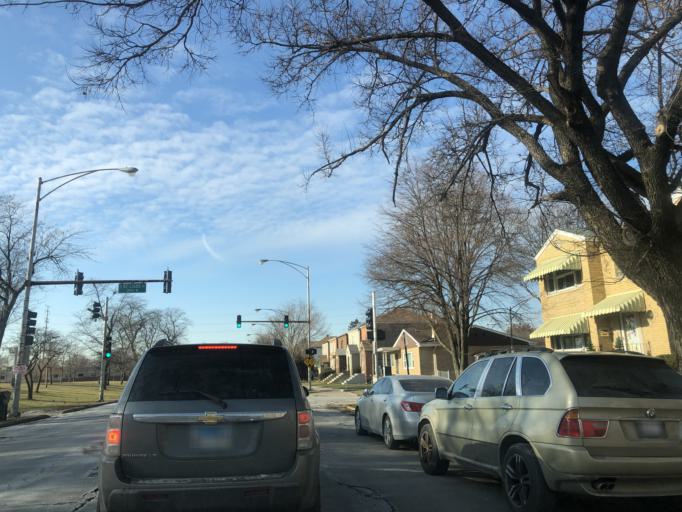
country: US
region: Illinois
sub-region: Cook County
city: Hometown
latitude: 41.7716
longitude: -87.7098
